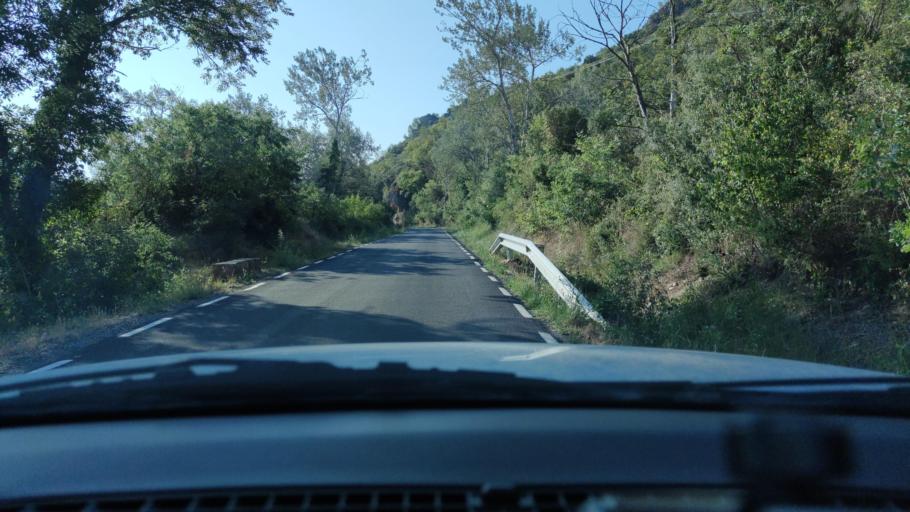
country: ES
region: Catalonia
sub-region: Provincia de Lleida
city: Camarasa
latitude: 41.8705
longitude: 0.8598
